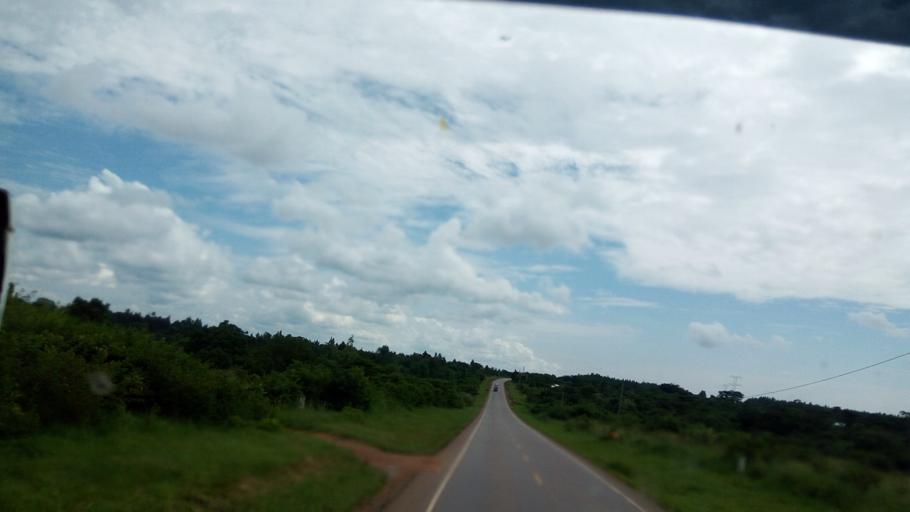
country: UG
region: Central Region
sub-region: Nakasongola District
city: Nakasongola
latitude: 1.1800
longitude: 32.4618
